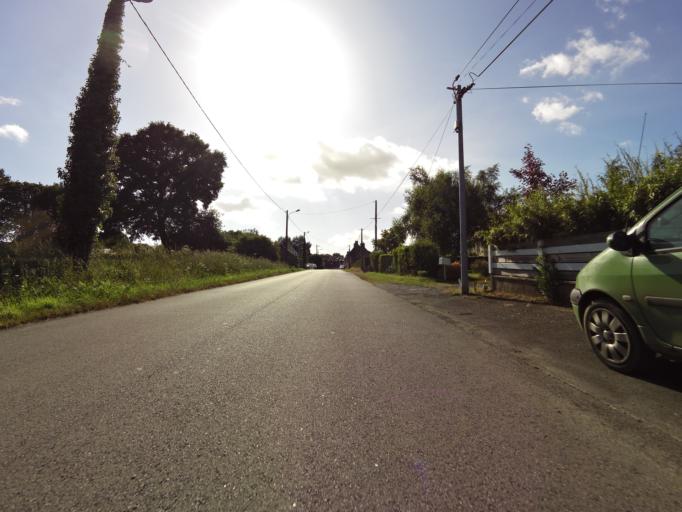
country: FR
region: Brittany
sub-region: Departement du Morbihan
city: Pluherlin
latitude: 47.6977
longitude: -2.3492
